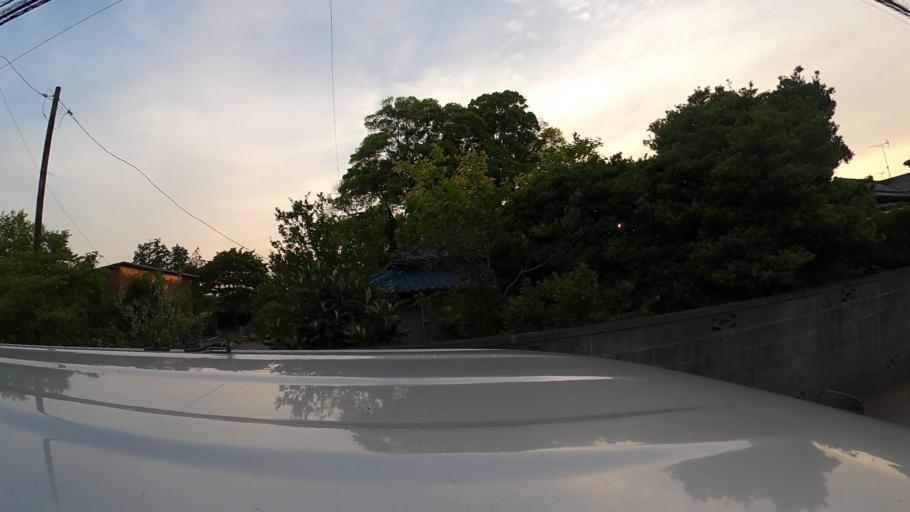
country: JP
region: Ibaraki
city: Ushiku
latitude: 36.0155
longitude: 140.1018
